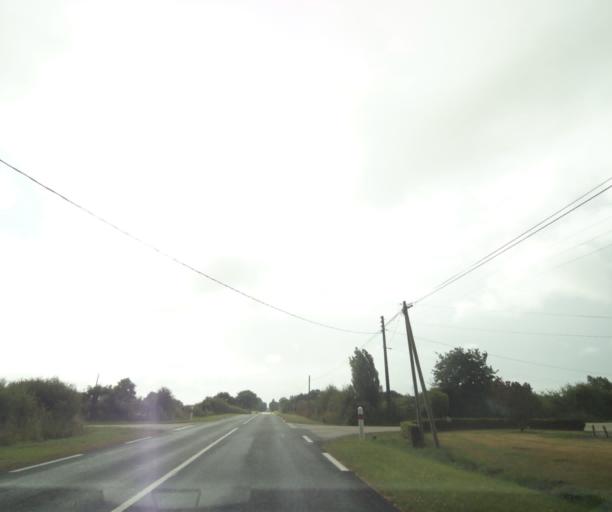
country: FR
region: Pays de la Loire
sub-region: Departement de la Vendee
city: Avrille
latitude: 46.4655
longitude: -1.4704
